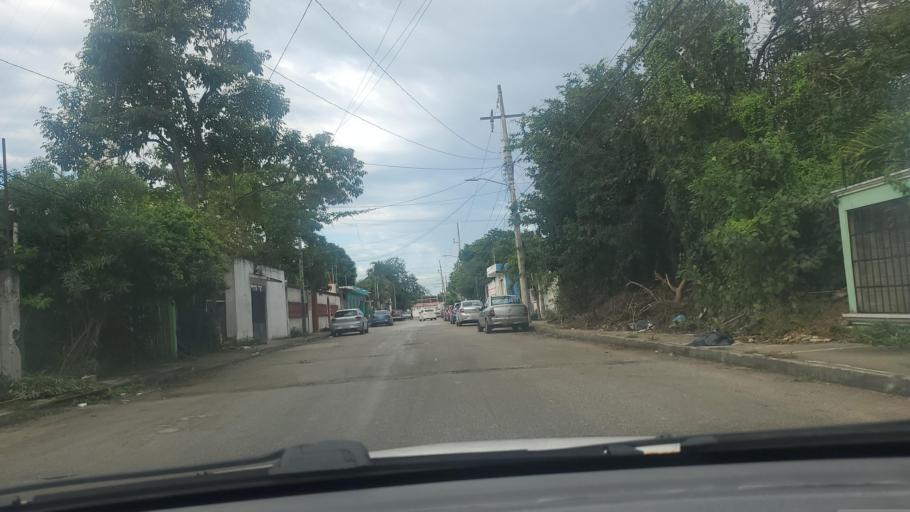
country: MX
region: Quintana Roo
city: Tulum
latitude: 20.2115
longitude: -87.4662
